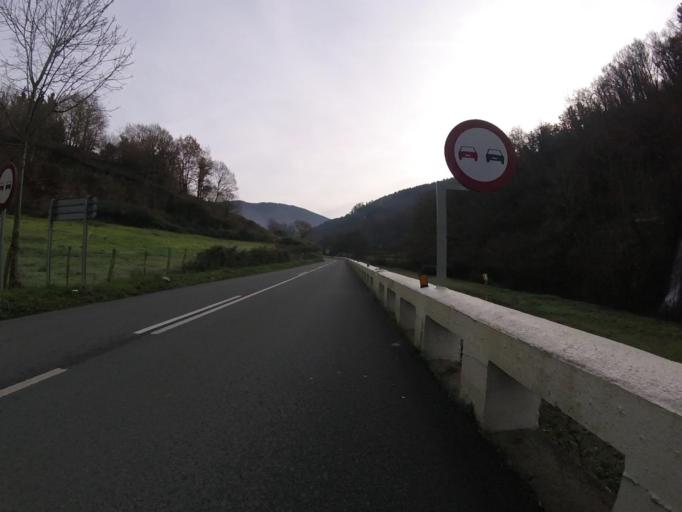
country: ES
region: Basque Country
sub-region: Provincia de Guipuzcoa
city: Berrobi
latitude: 43.1438
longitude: -2.0199
